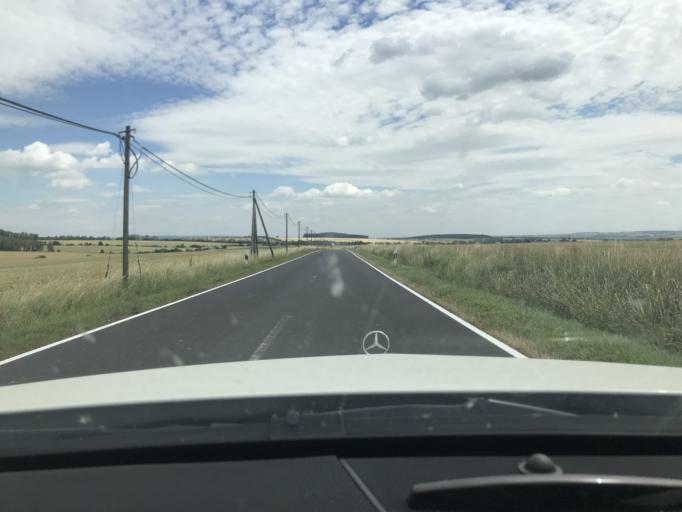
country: DE
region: Thuringia
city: Urbach
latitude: 51.3022
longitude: 10.5856
